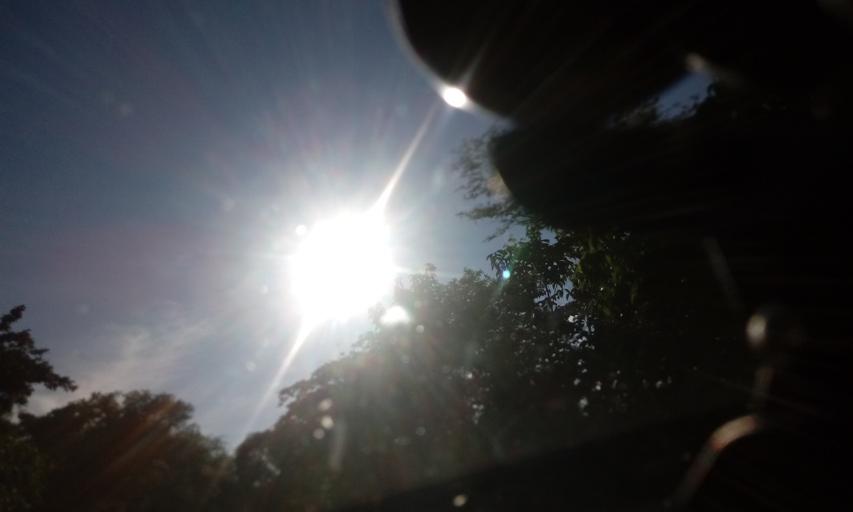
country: BR
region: Bahia
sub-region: Riacho De Santana
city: Riacho de Santana
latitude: -13.8563
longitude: -42.7751
